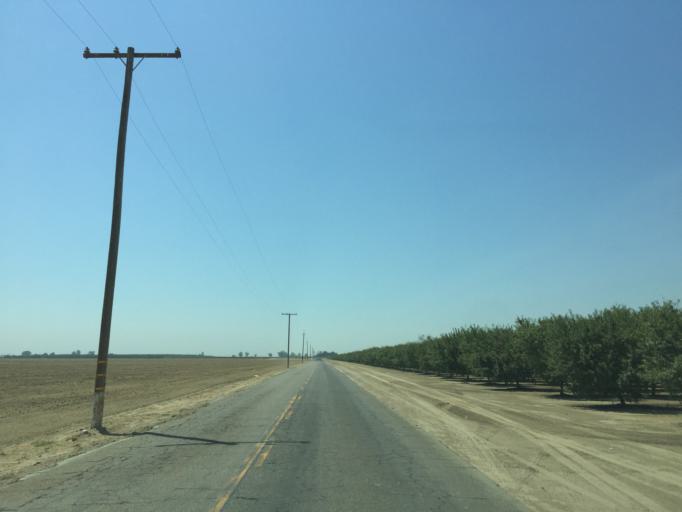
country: US
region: California
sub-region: Tulare County
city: Goshen
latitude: 36.3708
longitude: -119.4049
